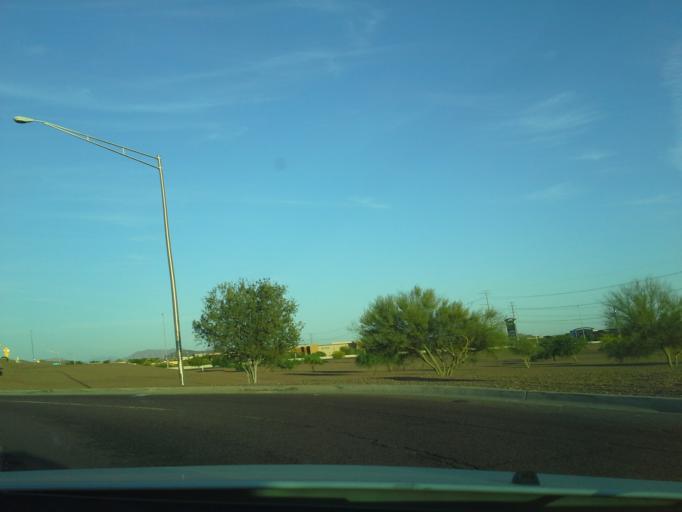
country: US
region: Arizona
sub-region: Maricopa County
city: Anthem
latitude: 33.7127
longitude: -112.1203
